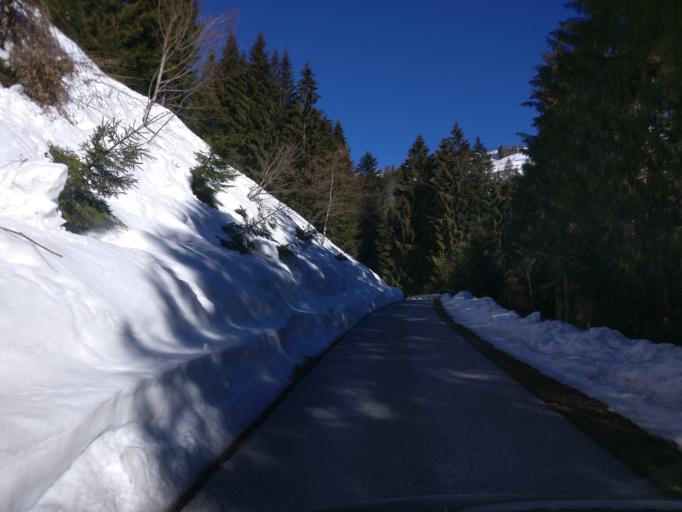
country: AT
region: Salzburg
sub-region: Politischer Bezirk Sankt Johann im Pongau
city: Wagrain
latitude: 47.3374
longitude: 13.2503
